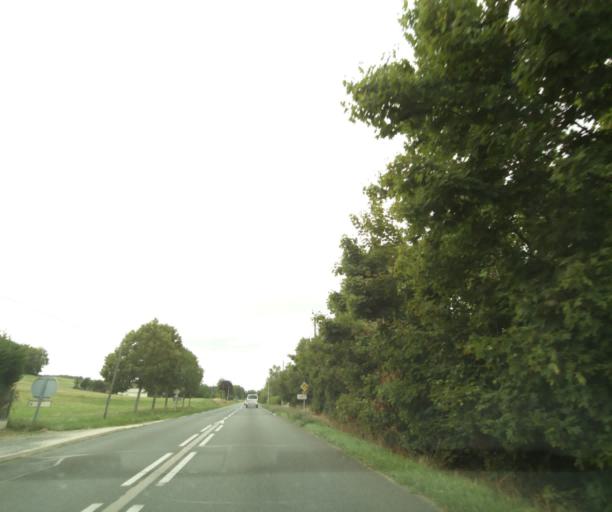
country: FR
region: Centre
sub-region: Departement d'Indre-et-Loire
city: Perrusson
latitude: 47.0611
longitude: 1.0828
